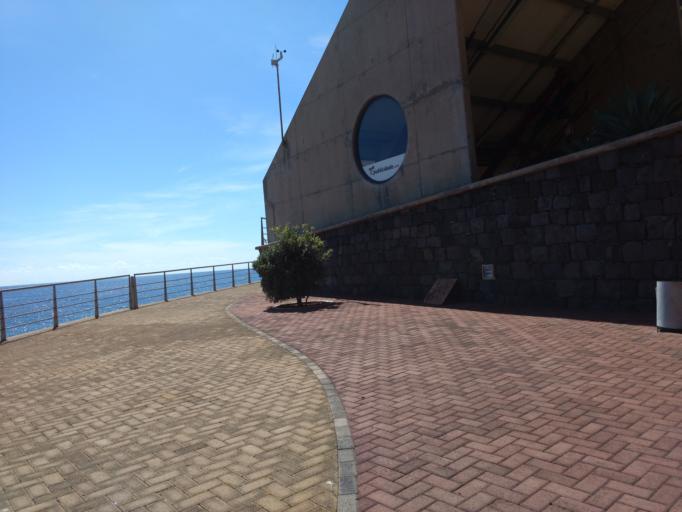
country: PT
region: Madeira
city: Canico
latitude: 32.6386
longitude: -16.8531
